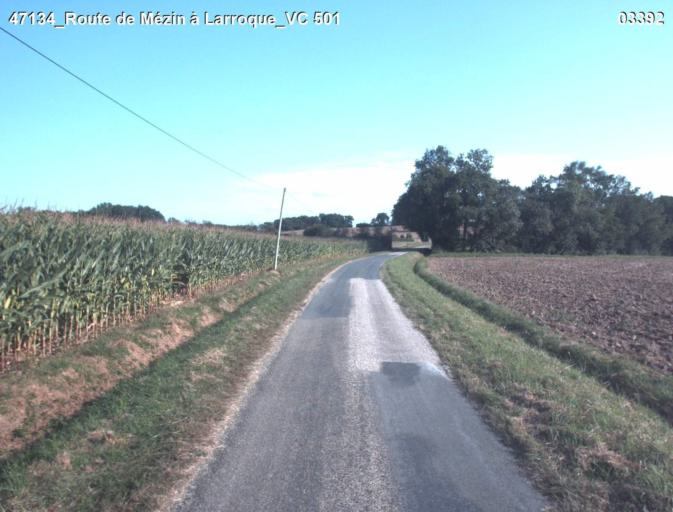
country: FR
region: Aquitaine
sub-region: Departement du Lot-et-Garonne
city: Mezin
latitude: 44.0252
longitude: 0.2695
